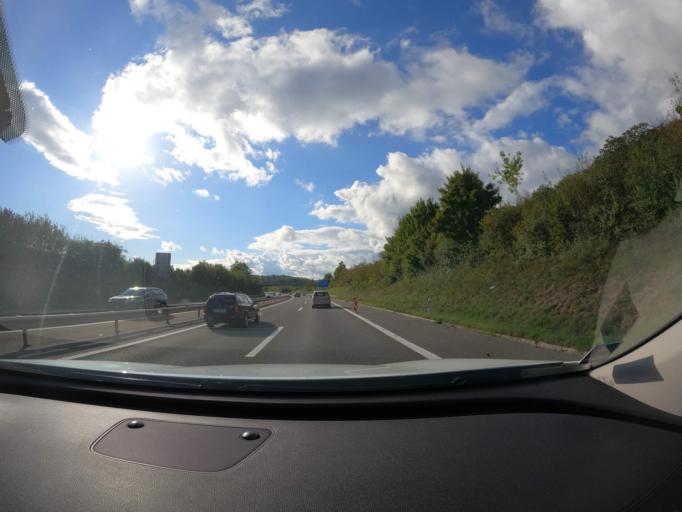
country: CH
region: Aargau
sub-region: Bezirk Brugg
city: Hausen
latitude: 47.4527
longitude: 8.2268
